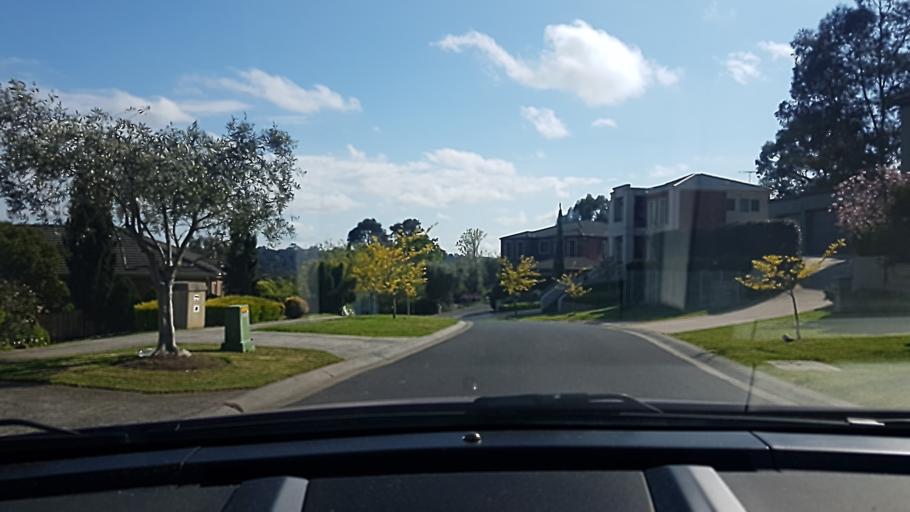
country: AU
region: Victoria
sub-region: Manningham
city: Templestowe Lower
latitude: -37.7589
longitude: 145.1157
